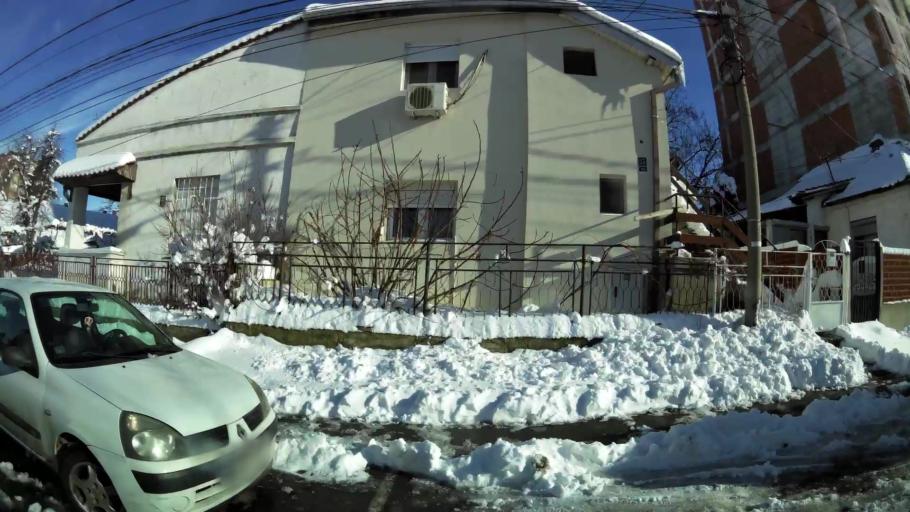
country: RS
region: Central Serbia
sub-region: Belgrade
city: Palilula
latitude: 44.7913
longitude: 20.5107
